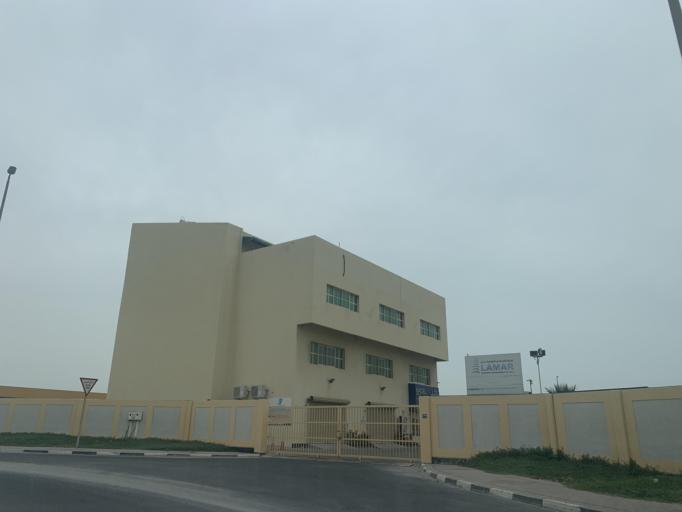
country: BH
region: Muharraq
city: Al Hadd
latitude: 26.2150
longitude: 50.6702
